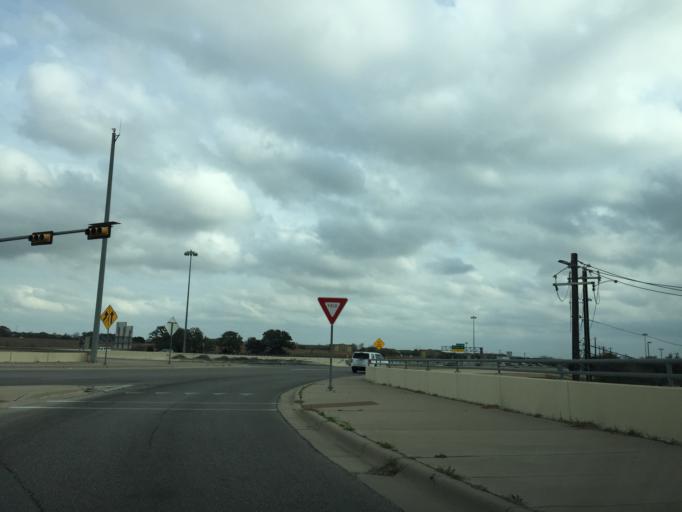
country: US
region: Texas
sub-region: Travis County
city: Wells Branch
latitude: 30.3992
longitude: -97.6742
